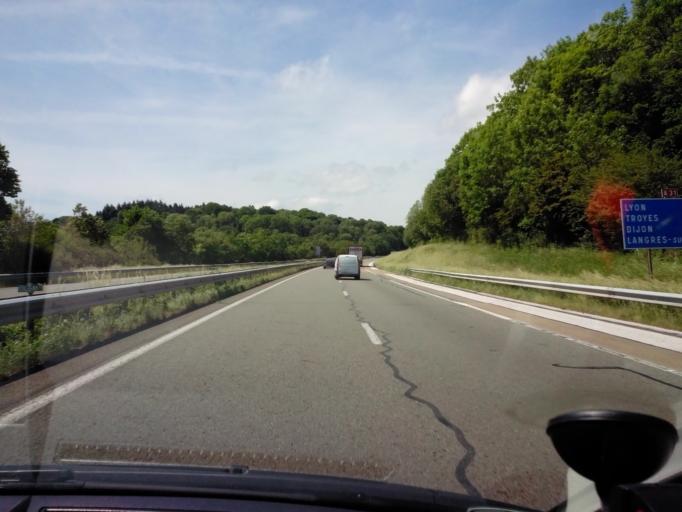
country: FR
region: Champagne-Ardenne
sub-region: Departement de la Haute-Marne
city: Avrecourt
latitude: 47.9678
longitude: 5.4884
